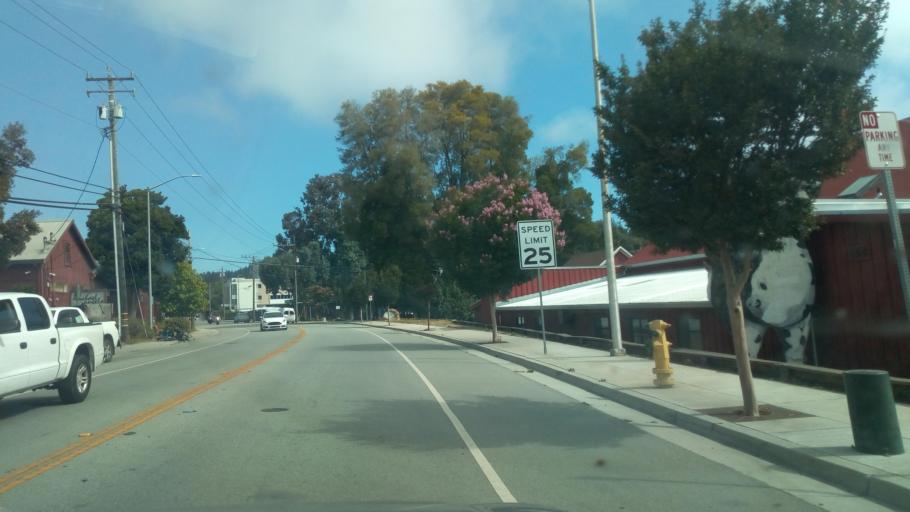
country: US
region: California
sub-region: Santa Cruz County
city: Santa Cruz
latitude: 36.9874
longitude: -122.0302
